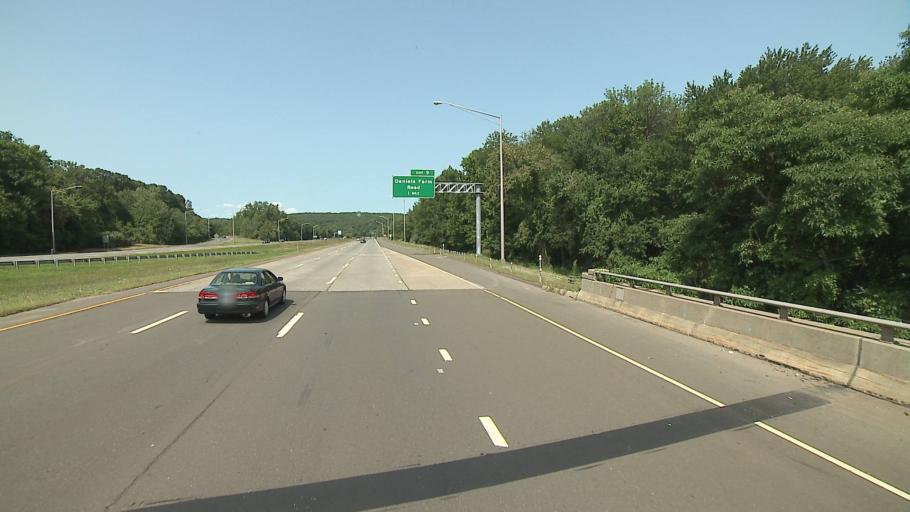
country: US
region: Connecticut
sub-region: Fairfield County
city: Trumbull
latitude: 41.2372
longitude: -73.1903
